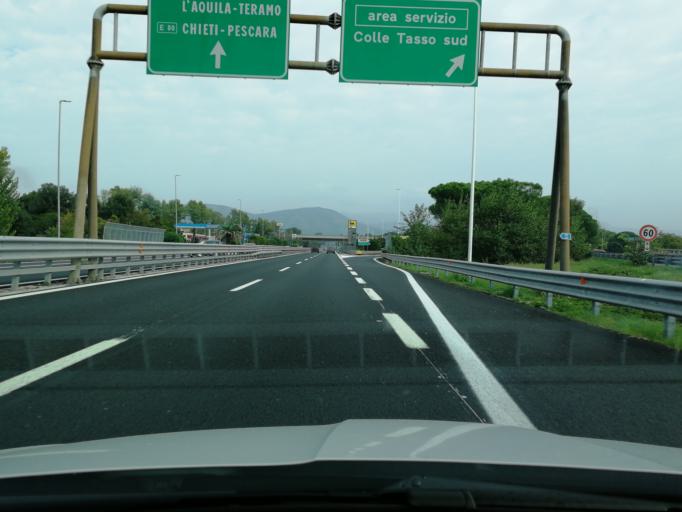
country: IT
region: Latium
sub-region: Citta metropolitana di Roma Capitale
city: Corcolle
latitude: 41.9272
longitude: 12.7358
